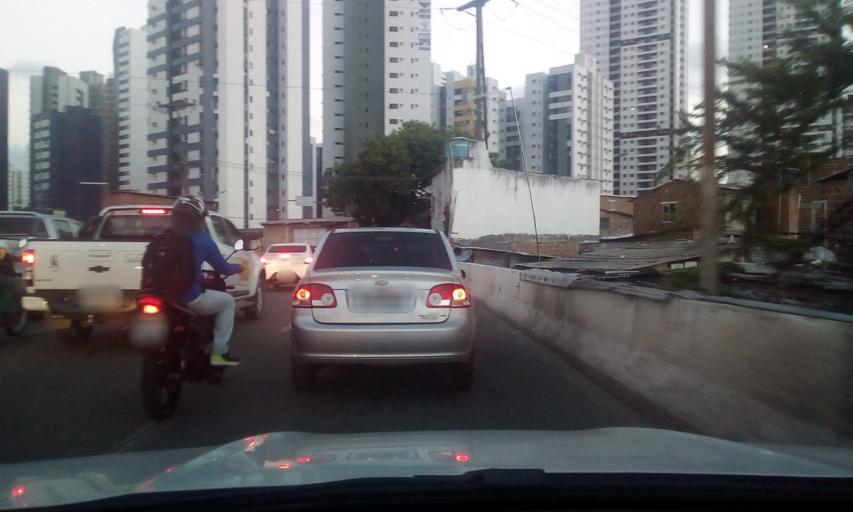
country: BR
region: Pernambuco
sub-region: Recife
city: Recife
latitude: -8.1239
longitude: -34.9096
